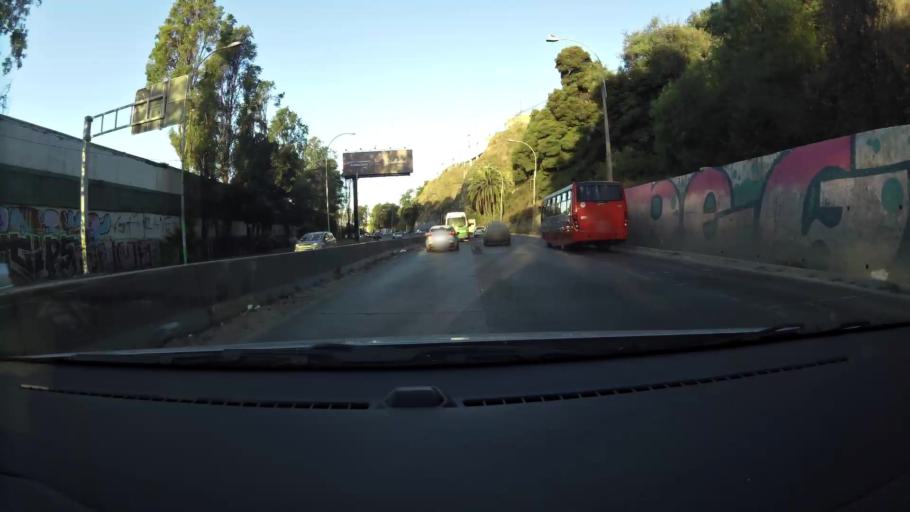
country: CL
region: Valparaiso
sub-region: Provincia de Valparaiso
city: Valparaiso
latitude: -33.0396
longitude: -71.6039
